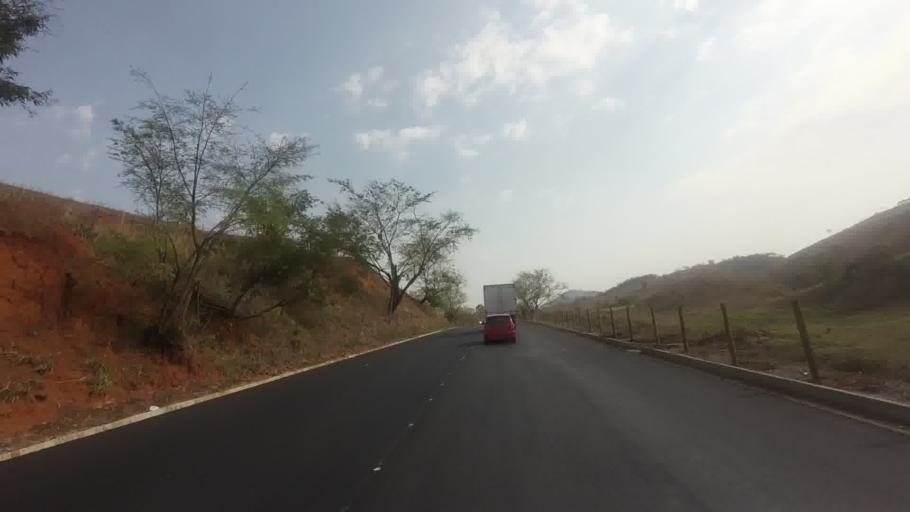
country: BR
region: Rio de Janeiro
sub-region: Bom Jesus Do Itabapoana
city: Bom Jesus do Itabapoana
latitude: -21.1774
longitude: -41.6847
